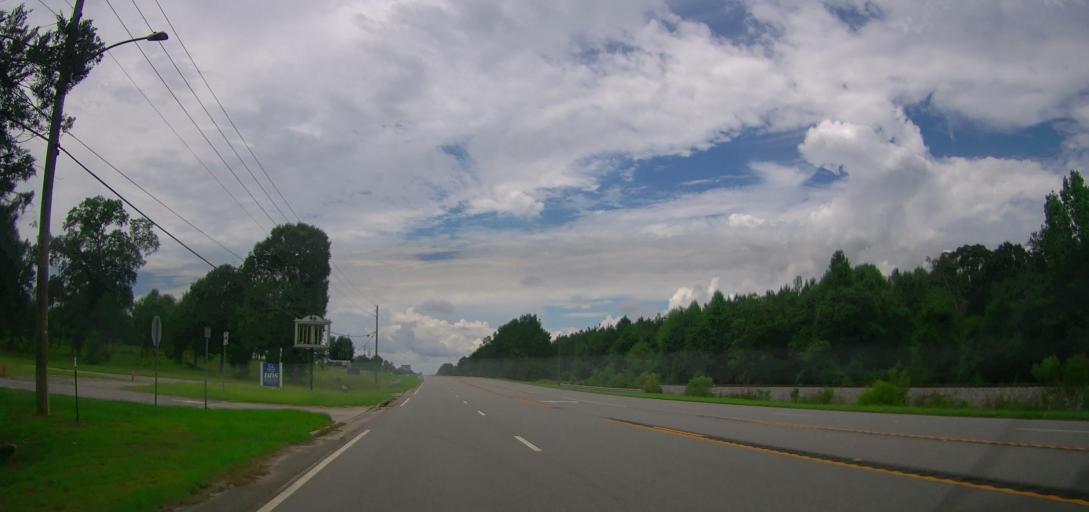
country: US
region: Georgia
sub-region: Telfair County
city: Helena
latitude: 32.0803
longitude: -82.9233
